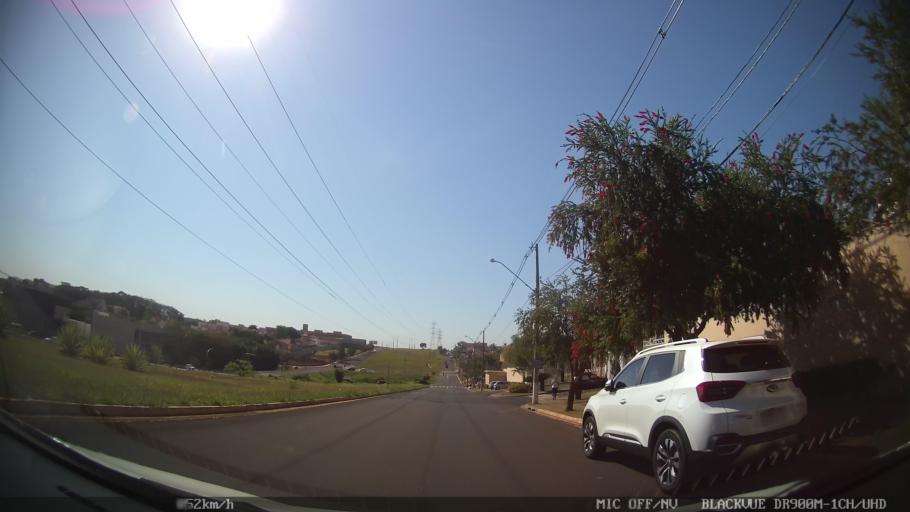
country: BR
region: Sao Paulo
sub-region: Ribeirao Preto
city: Ribeirao Preto
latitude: -21.2195
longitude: -47.7933
